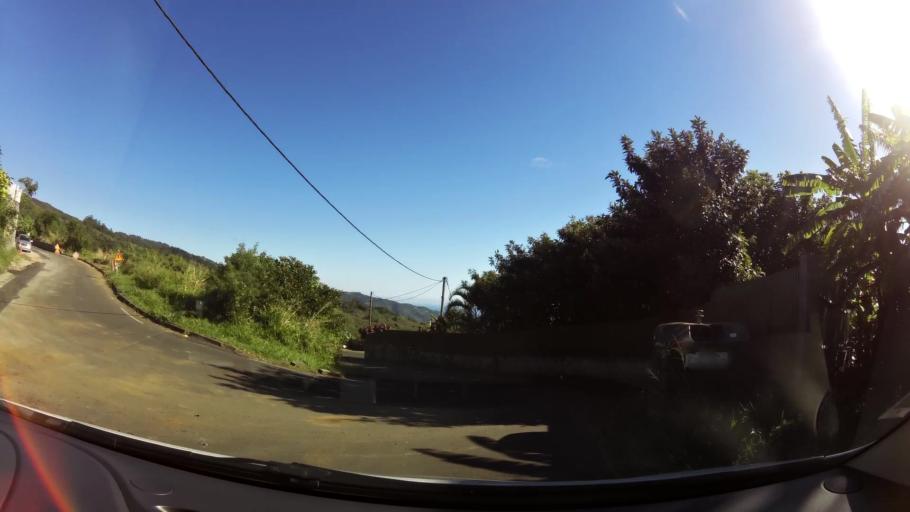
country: RE
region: Reunion
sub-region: Reunion
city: Saint-Denis
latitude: -20.9282
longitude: 55.4726
